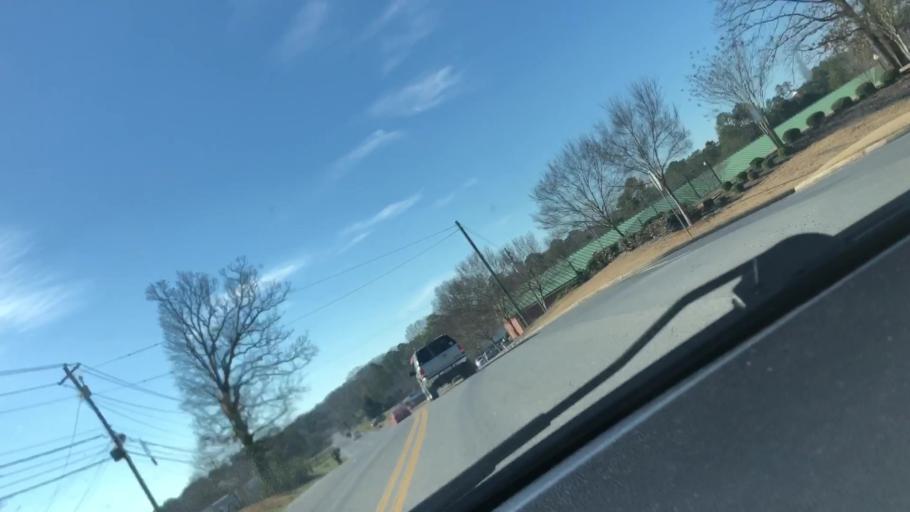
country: US
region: Georgia
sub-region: Bartow County
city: Cartersville
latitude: 34.2230
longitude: -84.8137
